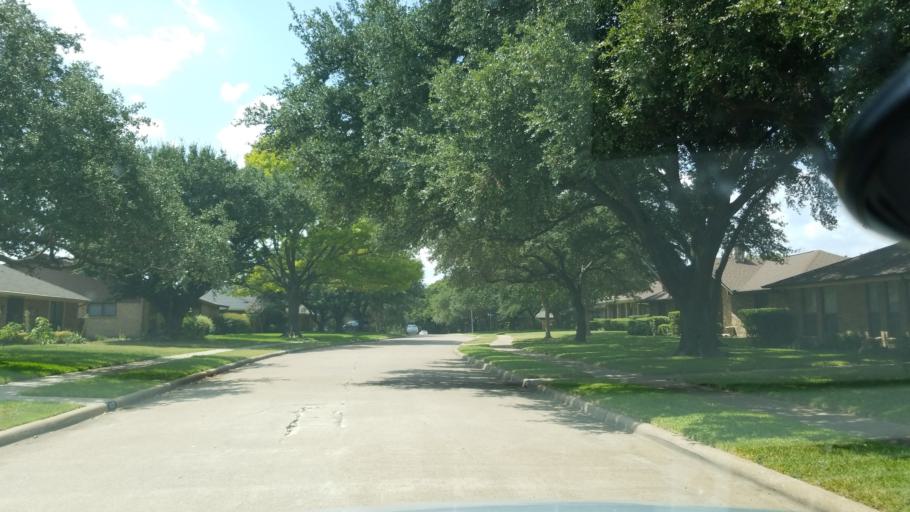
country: US
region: Texas
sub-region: Dallas County
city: Richardson
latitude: 32.9276
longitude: -96.7229
